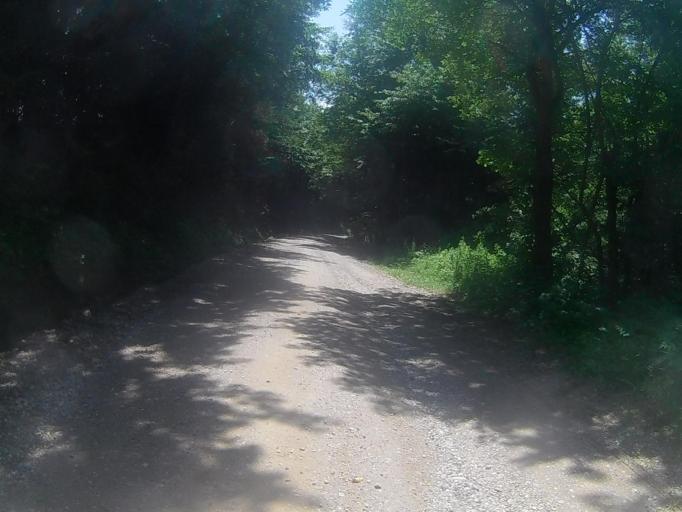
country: SI
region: Ruse
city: Bistrica ob Dravi
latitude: 46.5850
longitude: 15.5381
